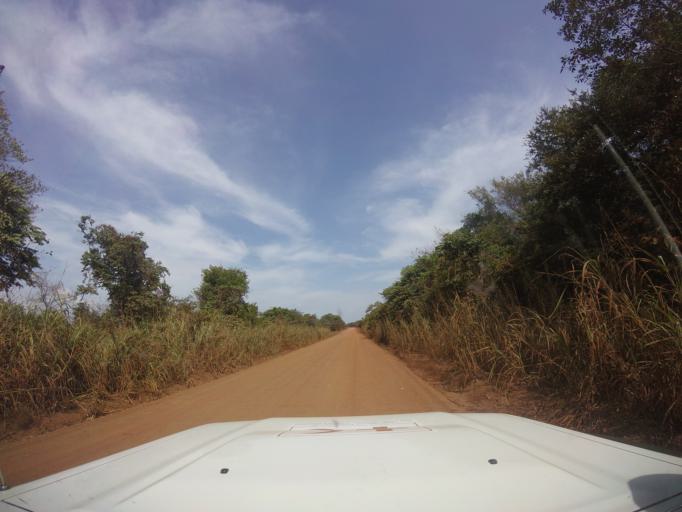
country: LR
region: Grand Cape Mount
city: Robertsport
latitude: 6.6903
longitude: -11.2610
